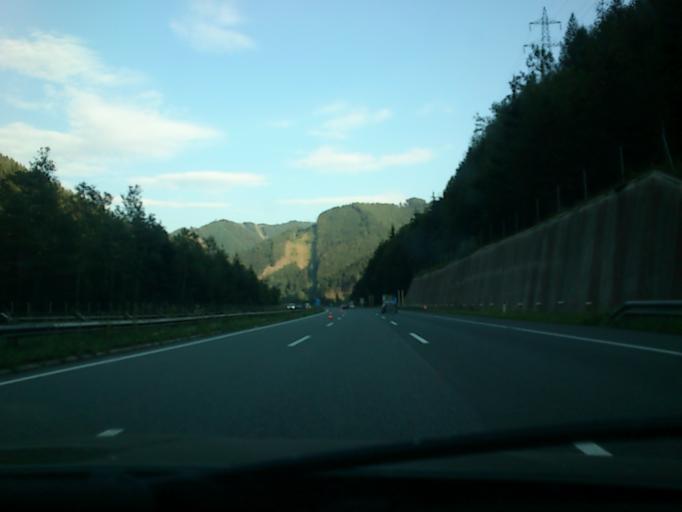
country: AT
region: Styria
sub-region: Politischer Bezirk Leoben
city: Sankt Michael in Obersteiermark
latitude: 47.3040
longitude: 15.0629
